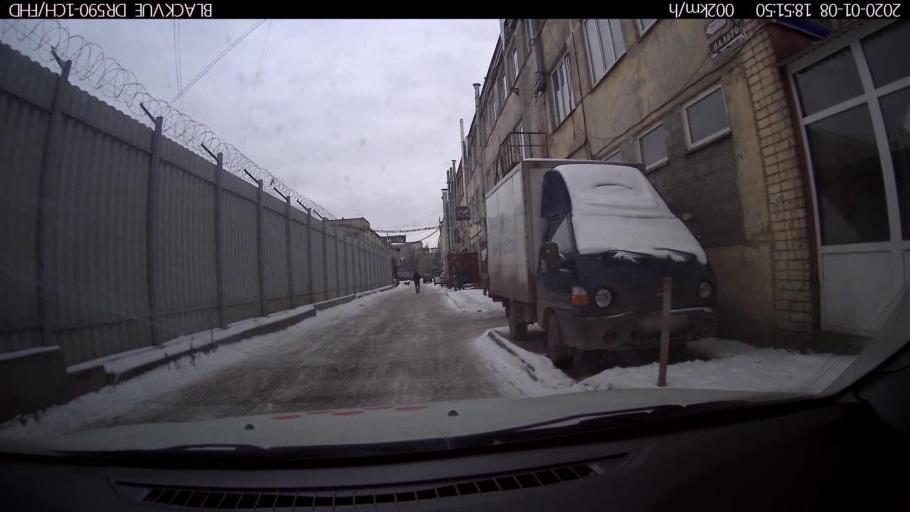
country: RU
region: Nizjnij Novgorod
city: Nizhniy Novgorod
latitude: 56.2706
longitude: 43.9408
